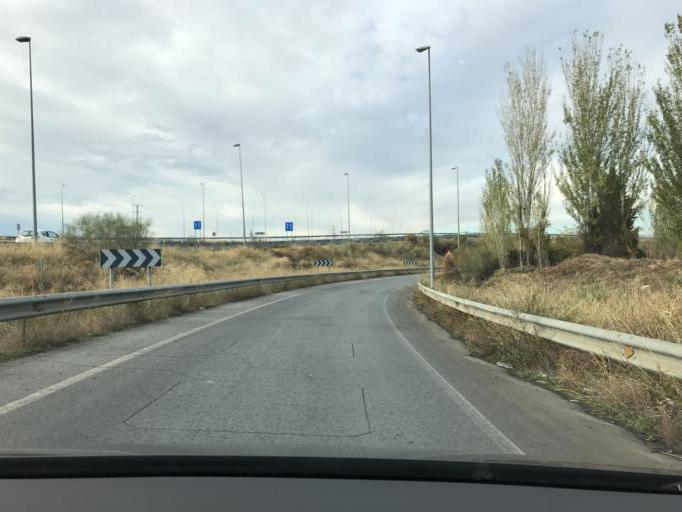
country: ES
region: Andalusia
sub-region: Provincia de Granada
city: Armilla
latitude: 37.1428
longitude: -3.6055
